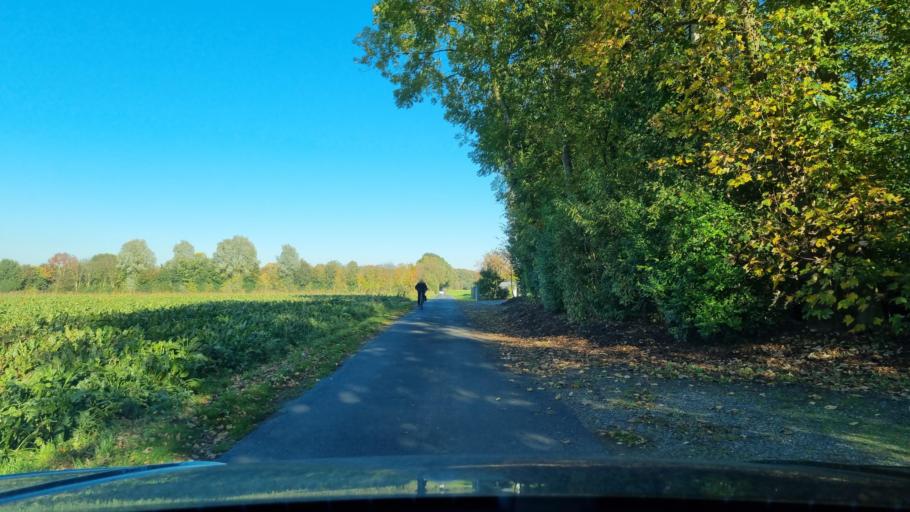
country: DE
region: North Rhine-Westphalia
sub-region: Regierungsbezirk Dusseldorf
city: Kranenburg
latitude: 51.7662
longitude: 6.0484
